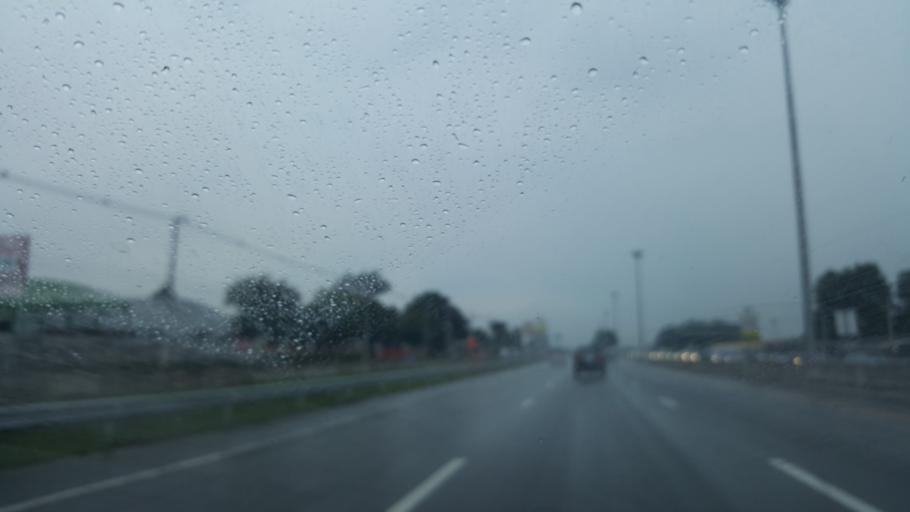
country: TH
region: Chon Buri
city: Ban Talat Bueng
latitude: 13.0617
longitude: 100.9962
